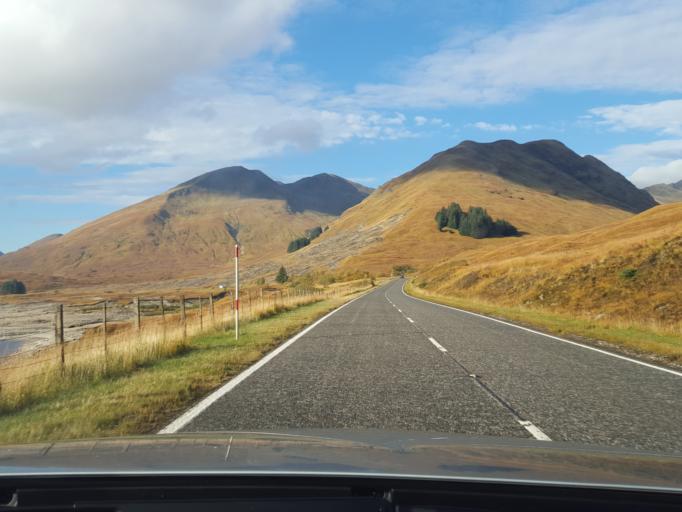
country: GB
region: Scotland
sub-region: Highland
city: Fort William
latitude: 57.1574
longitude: -5.1504
